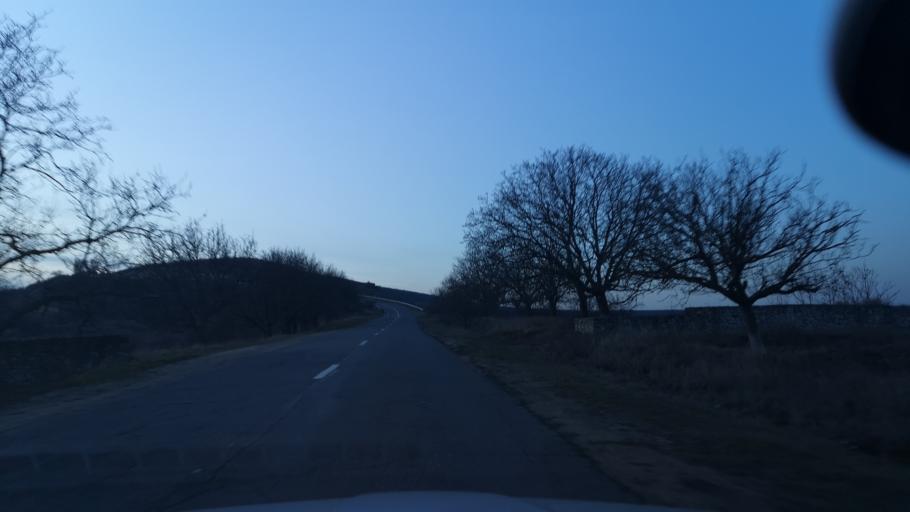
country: MD
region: Telenesti
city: Cocieri
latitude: 47.3096
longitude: 28.9730
